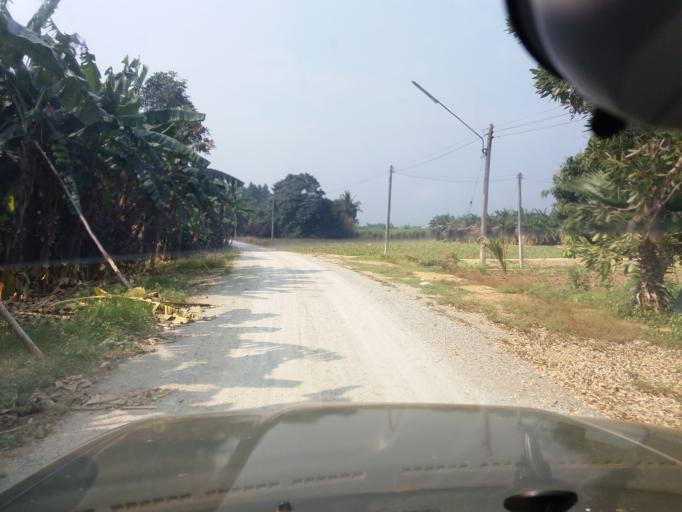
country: TH
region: Sing Buri
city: Bang Racham
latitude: 14.8981
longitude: 100.2129
